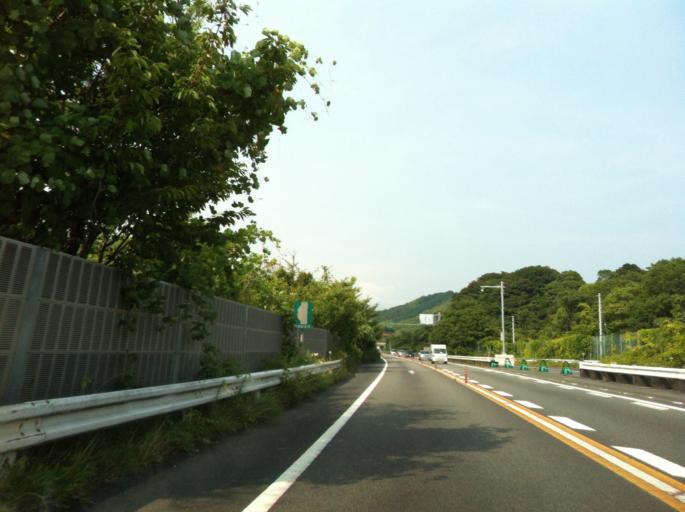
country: JP
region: Shizuoka
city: Fujieda
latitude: 34.8742
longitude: 138.2311
